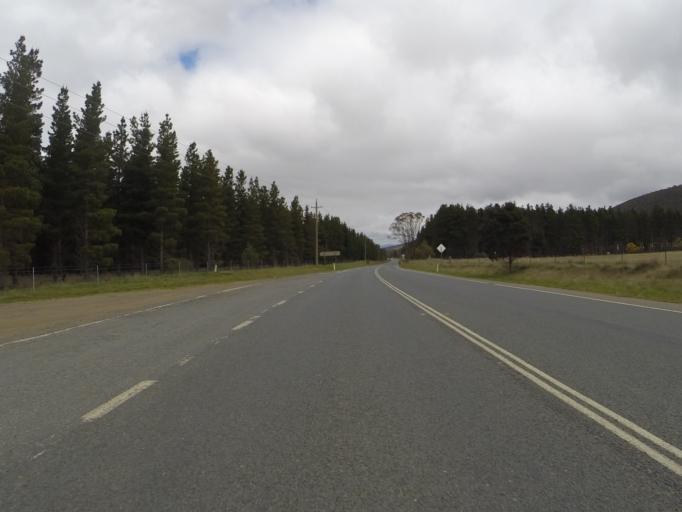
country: AU
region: Australian Capital Territory
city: Canberra
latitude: -35.2376
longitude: 149.1975
